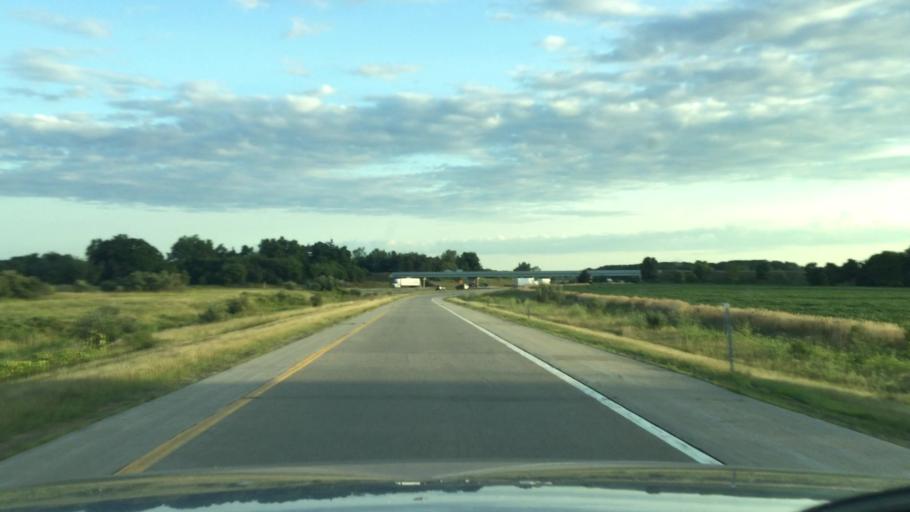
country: US
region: Michigan
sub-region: Clinton County
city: Bath
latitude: 42.8090
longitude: -84.5094
